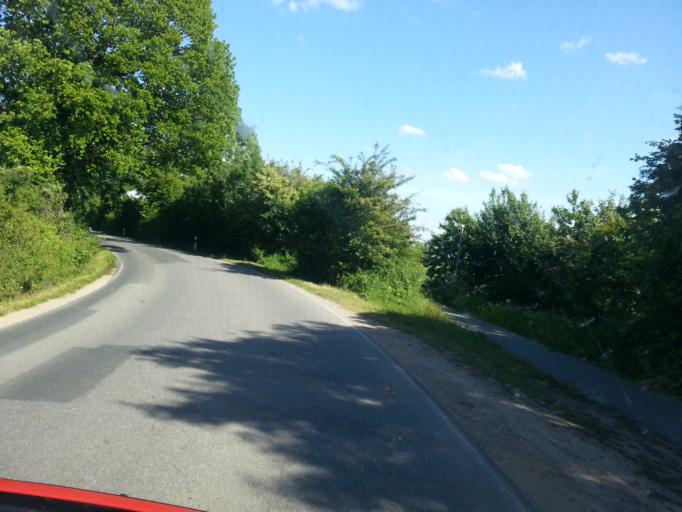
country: DE
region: Schleswig-Holstein
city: Ratekau
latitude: 53.9891
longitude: 10.7300
